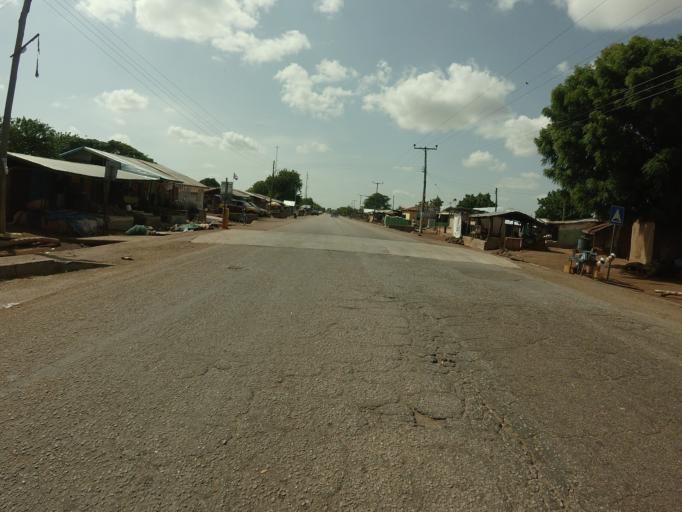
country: GH
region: Northern
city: Savelugu
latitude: 9.8675
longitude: -0.8711
